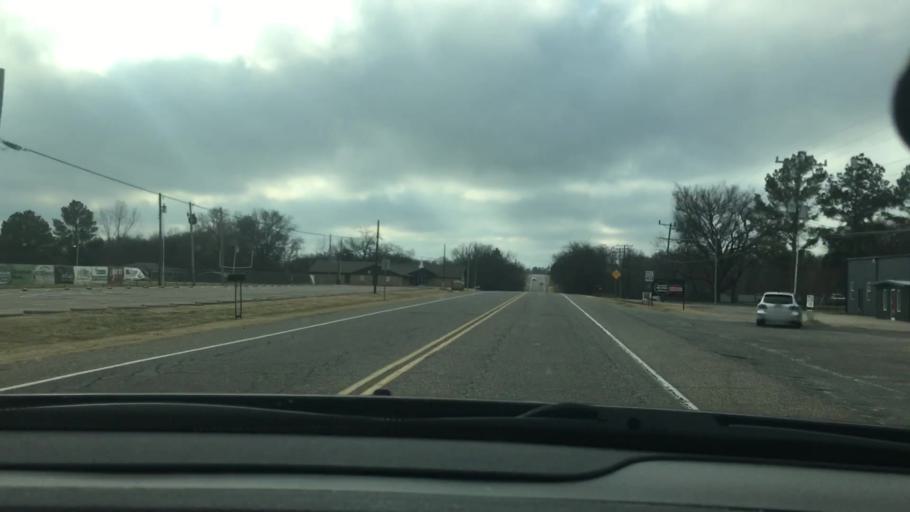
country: US
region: Oklahoma
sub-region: Bryan County
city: Durant
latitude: 34.0136
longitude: -96.3730
